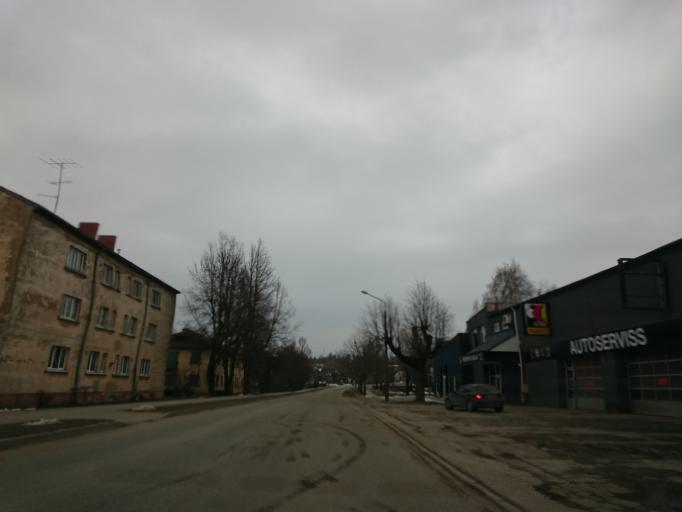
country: LV
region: Cesu Rajons
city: Cesis
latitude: 57.3205
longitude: 25.2638
